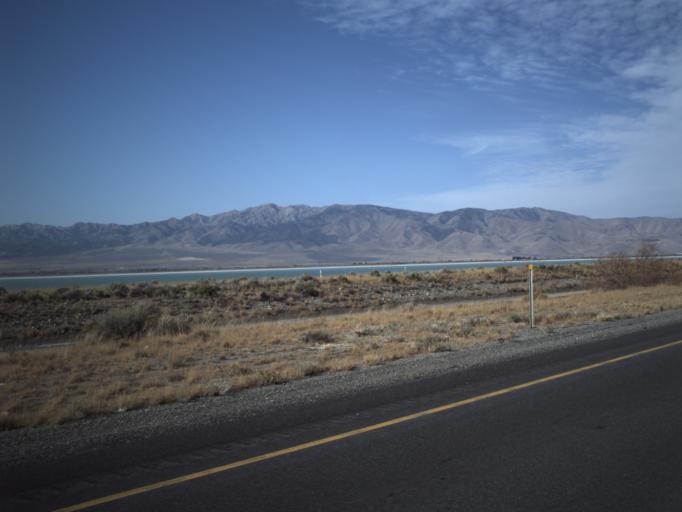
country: US
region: Utah
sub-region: Tooele County
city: Stansbury park
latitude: 40.6698
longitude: -112.3810
